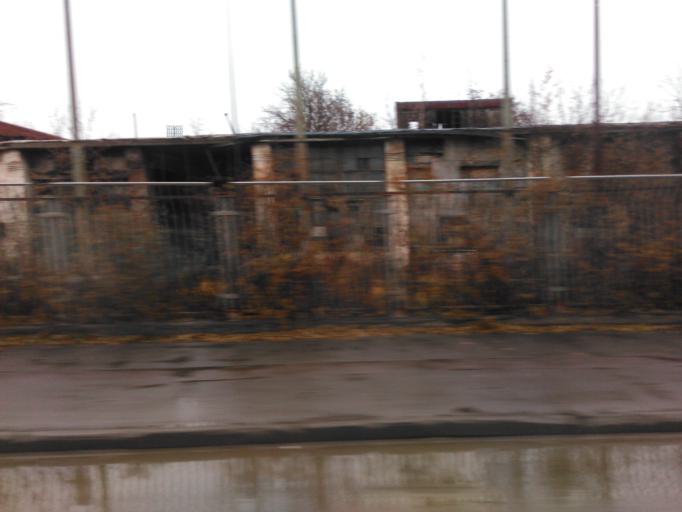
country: RU
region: Tatarstan
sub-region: Gorod Kazan'
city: Kazan
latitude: 55.7944
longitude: 49.0957
